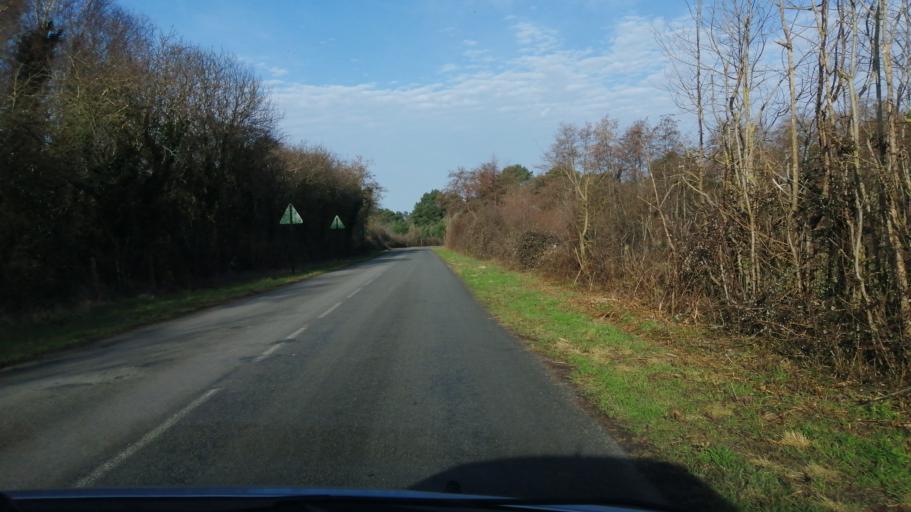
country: FR
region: Nord-Pas-de-Calais
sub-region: Departement du Pas-de-Calais
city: Dannes
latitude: 50.5903
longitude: 1.6058
